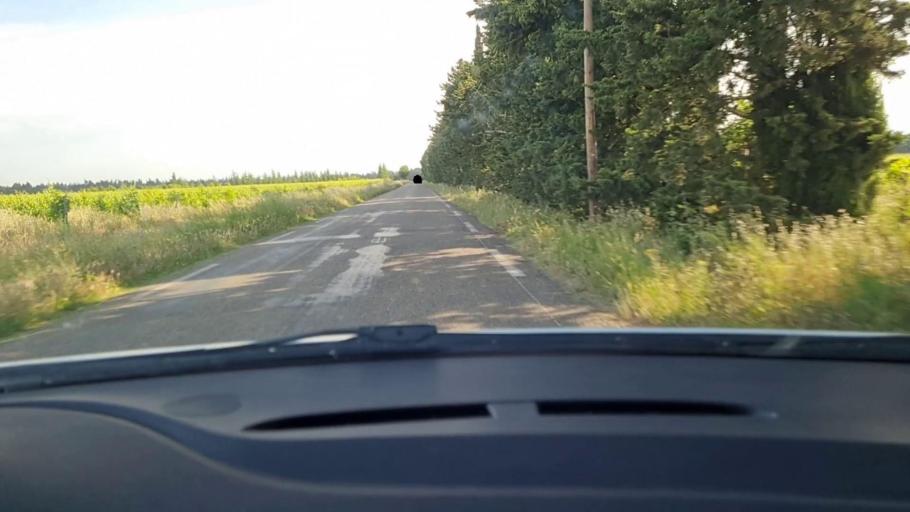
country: FR
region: Languedoc-Roussillon
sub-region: Departement du Gard
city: Bellegarde
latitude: 43.7833
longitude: 4.5245
